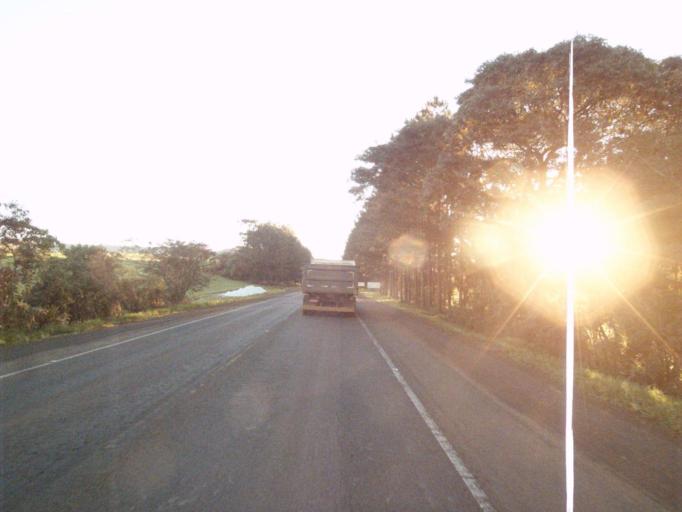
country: BR
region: Santa Catarina
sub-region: Sao Lourenco Do Oeste
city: Sao Lourenco dOeste
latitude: -26.8293
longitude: -53.1316
